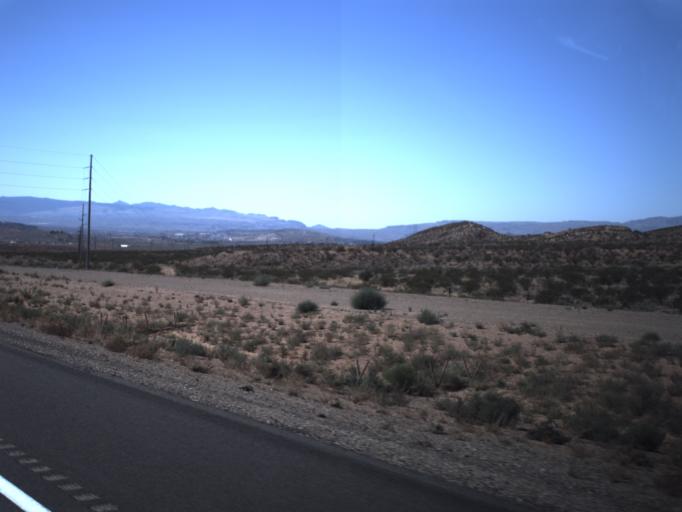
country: US
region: Utah
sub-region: Washington County
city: Washington
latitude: 37.0939
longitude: -113.4700
